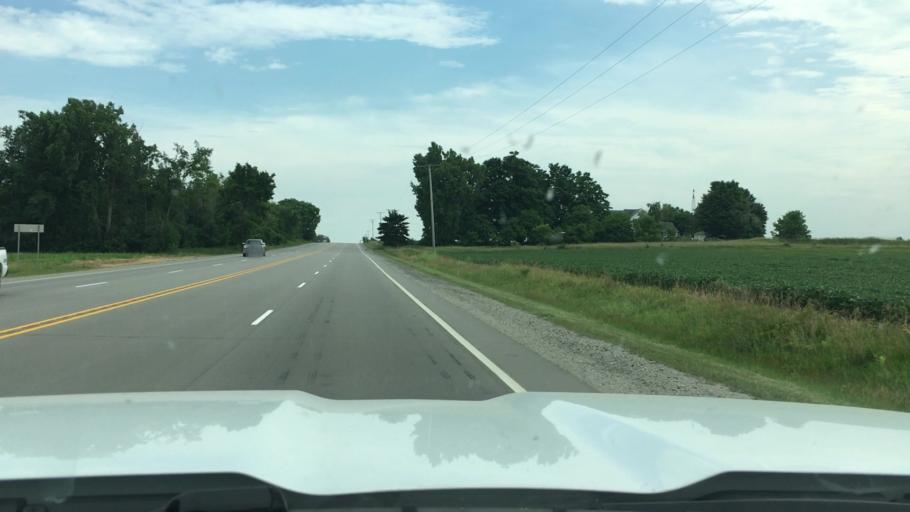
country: US
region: Michigan
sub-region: Sanilac County
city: Marlette
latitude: 43.3842
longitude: -83.0861
